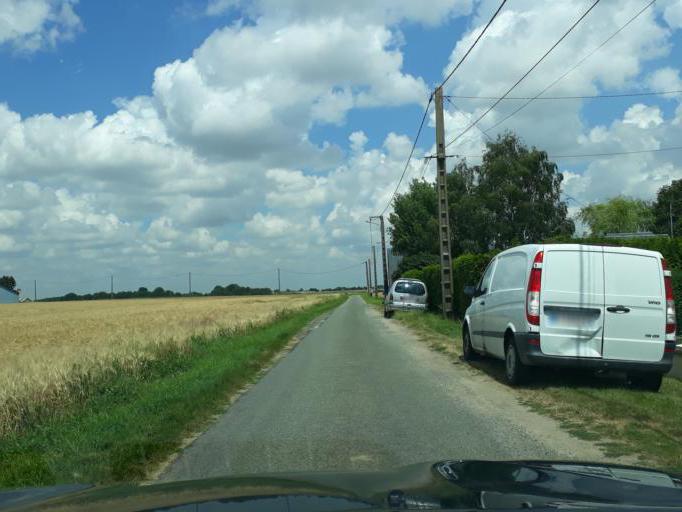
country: FR
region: Centre
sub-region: Departement du Loiret
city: Chevilly
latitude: 48.0382
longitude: 1.9086
